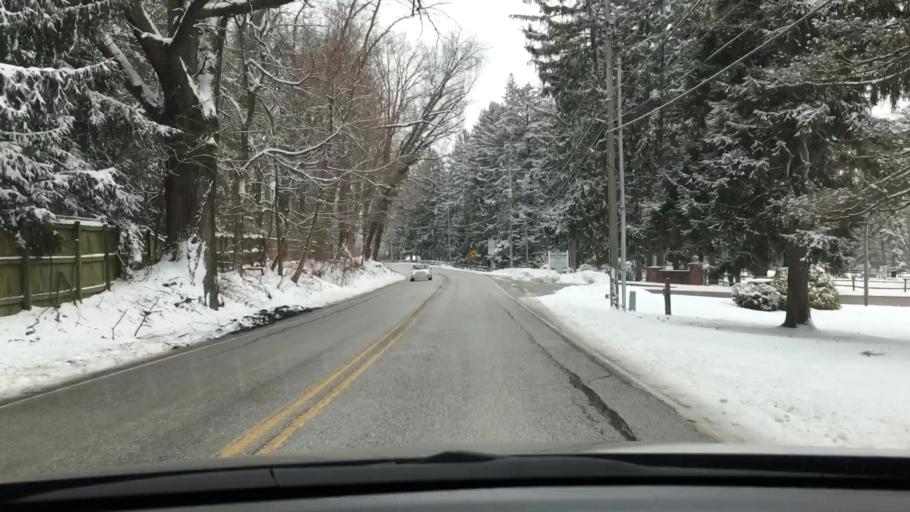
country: US
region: Pennsylvania
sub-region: York County
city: Grantley
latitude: 39.9367
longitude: -76.7261
